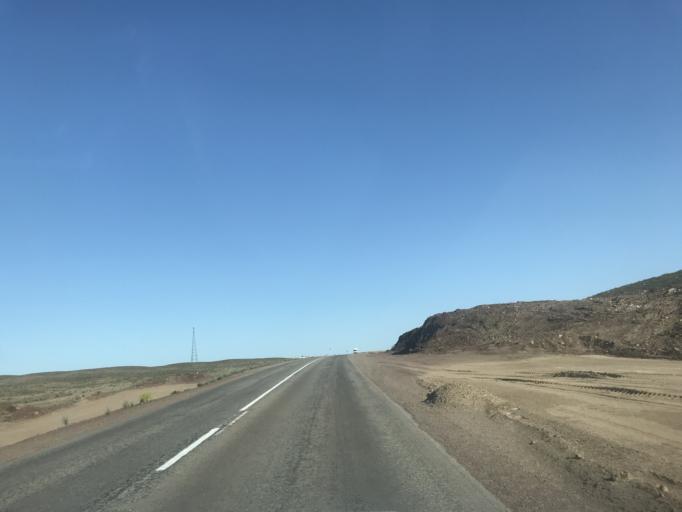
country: KZ
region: Zhambyl
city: Mynaral
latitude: 45.3328
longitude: 73.7236
